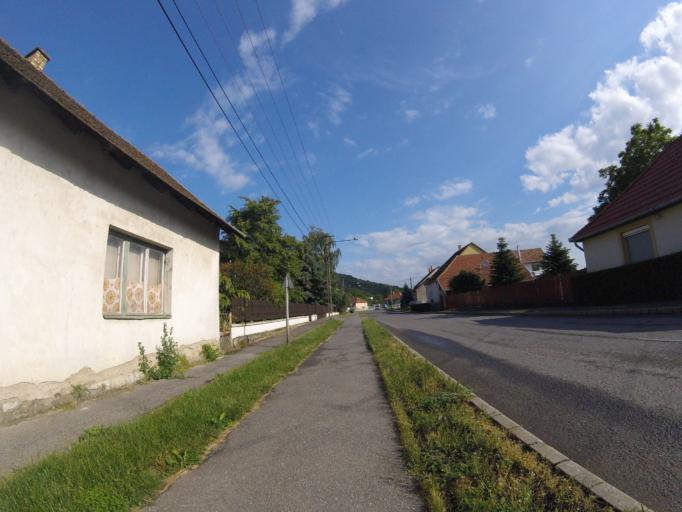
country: HU
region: Borsod-Abauj-Zemplen
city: Tokaj
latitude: 48.1097
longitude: 21.4106
